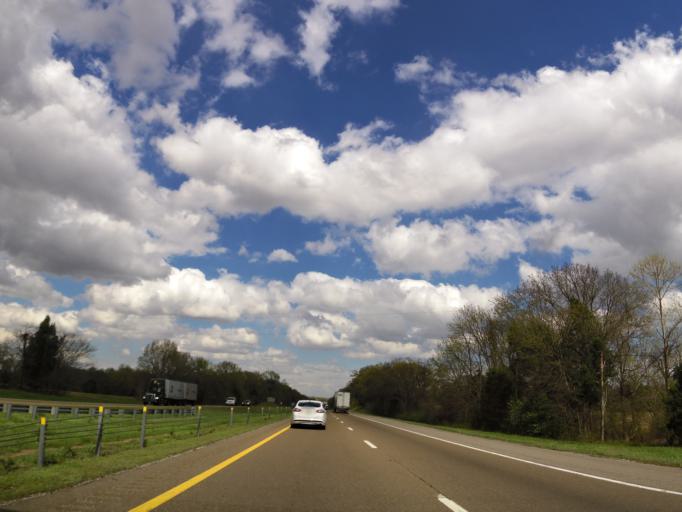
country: US
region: Tennessee
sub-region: Crockett County
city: Bells
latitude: 35.6024
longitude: -89.0409
